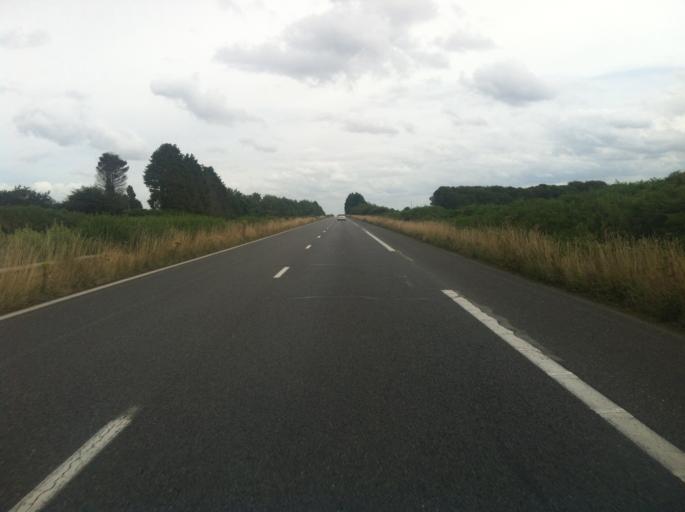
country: FR
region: Brittany
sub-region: Departement du Finistere
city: La Roche-Maurice
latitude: 48.4954
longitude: -4.2002
